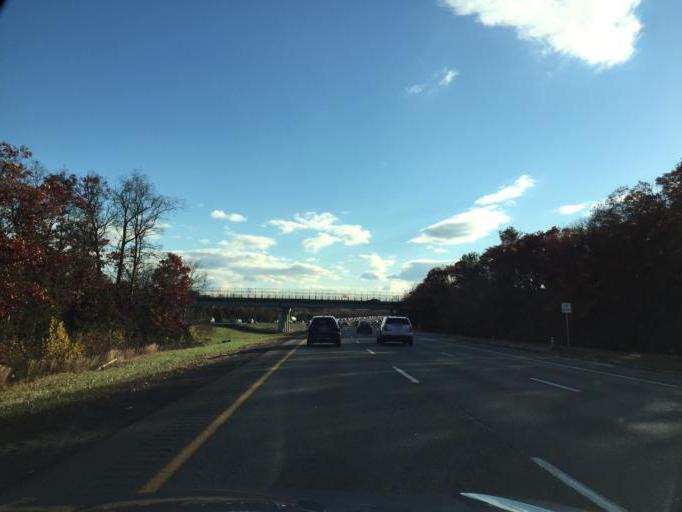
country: US
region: Massachusetts
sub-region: Bristol County
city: Attleboro
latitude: 41.9713
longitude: -71.2955
